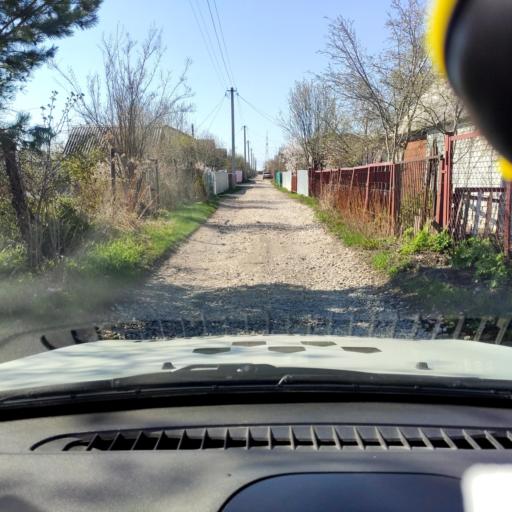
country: RU
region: Samara
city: Tol'yatti
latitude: 53.5946
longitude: 49.2939
